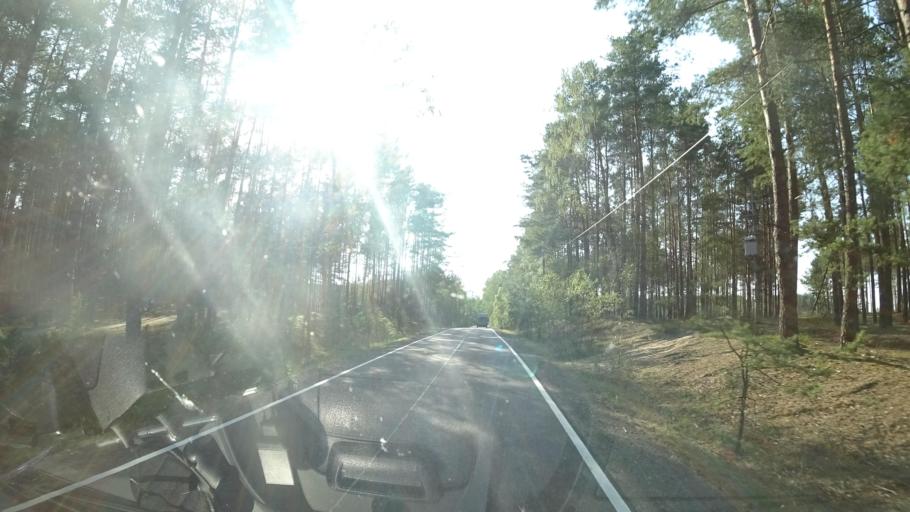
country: PL
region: Pomeranian Voivodeship
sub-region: Powiat chojnicki
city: Chojnice
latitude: 53.8545
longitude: 17.5592
